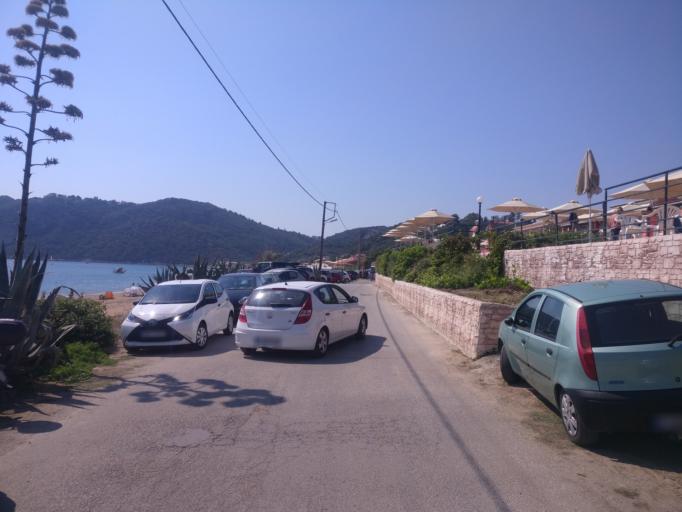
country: GR
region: Ionian Islands
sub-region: Nomos Kerkyras
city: Agios Georgis
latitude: 39.7193
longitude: 19.6766
